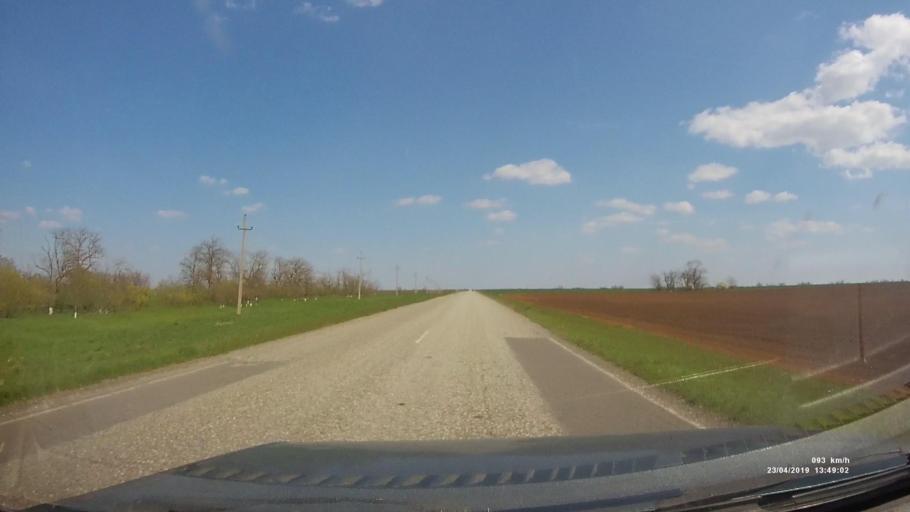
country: RU
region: Kalmykiya
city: Yashalta
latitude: 46.5993
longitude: 42.8863
